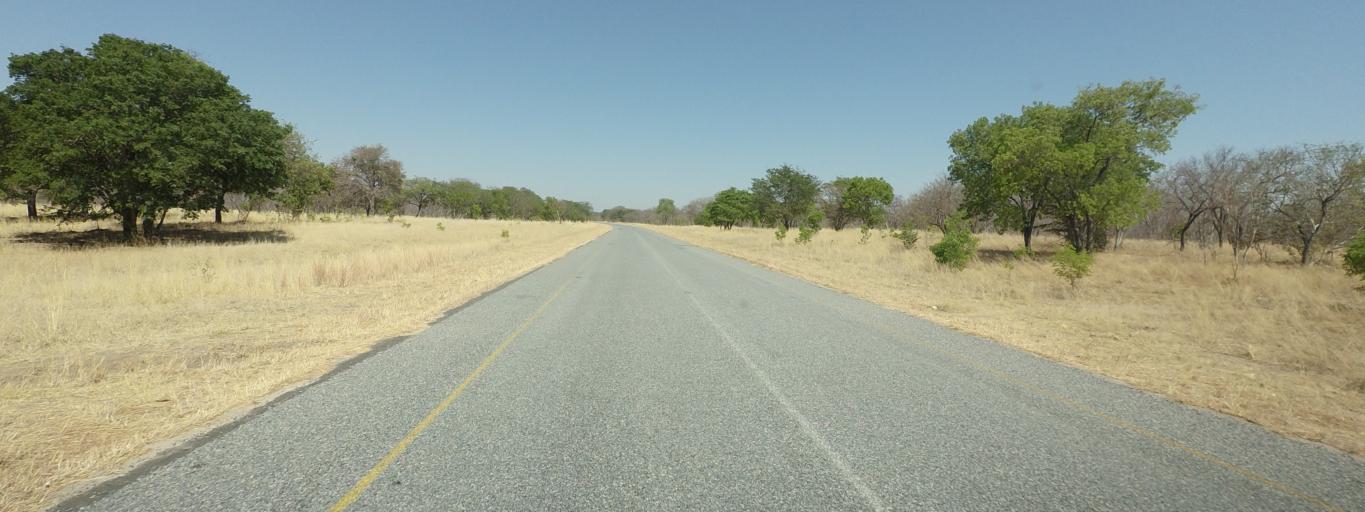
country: BW
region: North West
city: Kasane
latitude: -17.9222
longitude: 25.0367
